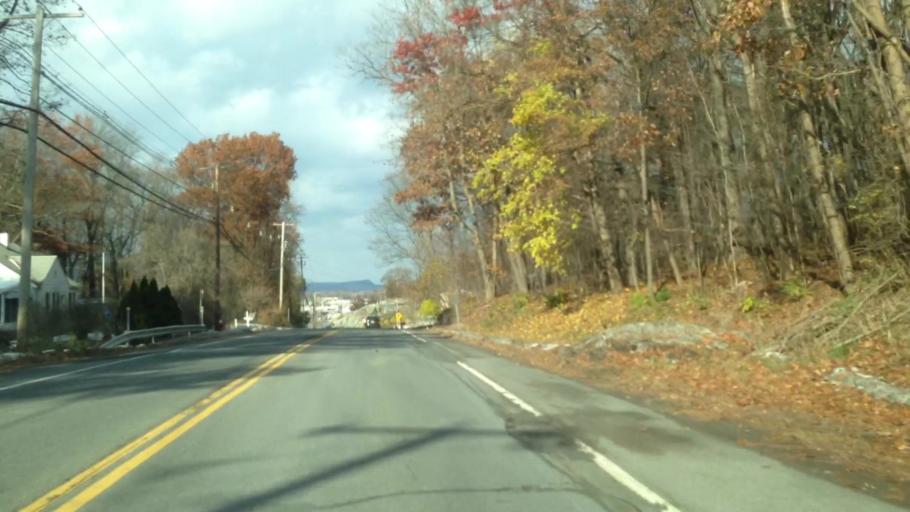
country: US
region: New York
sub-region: Ulster County
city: Lincoln Park
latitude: 41.9510
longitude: -73.9908
